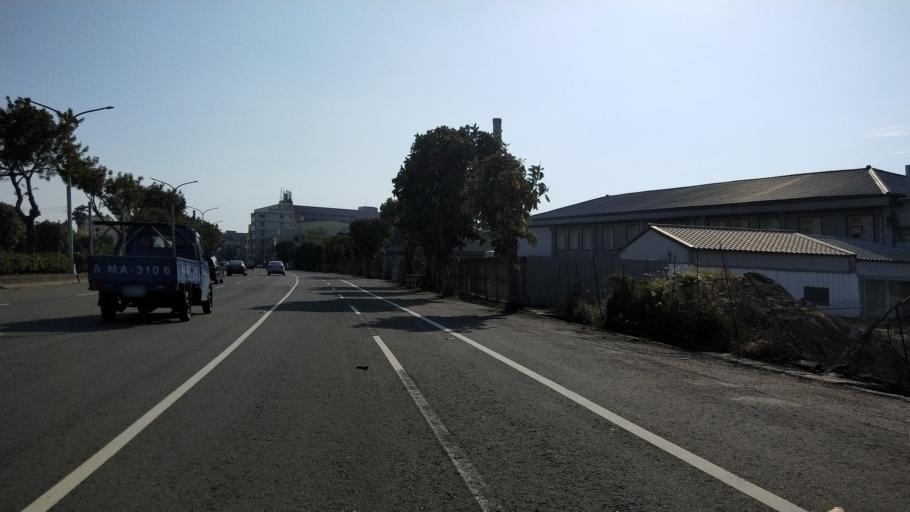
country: TW
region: Taiwan
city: Fengyuan
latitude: 24.2951
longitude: 120.5898
